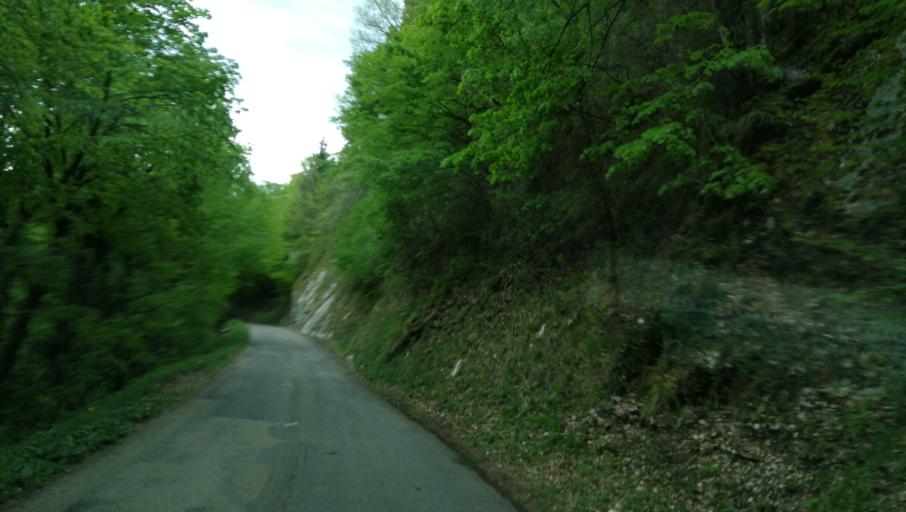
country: FR
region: Rhone-Alpes
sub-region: Departement de la Savoie
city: Chatillon
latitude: 45.7458
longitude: 5.8318
